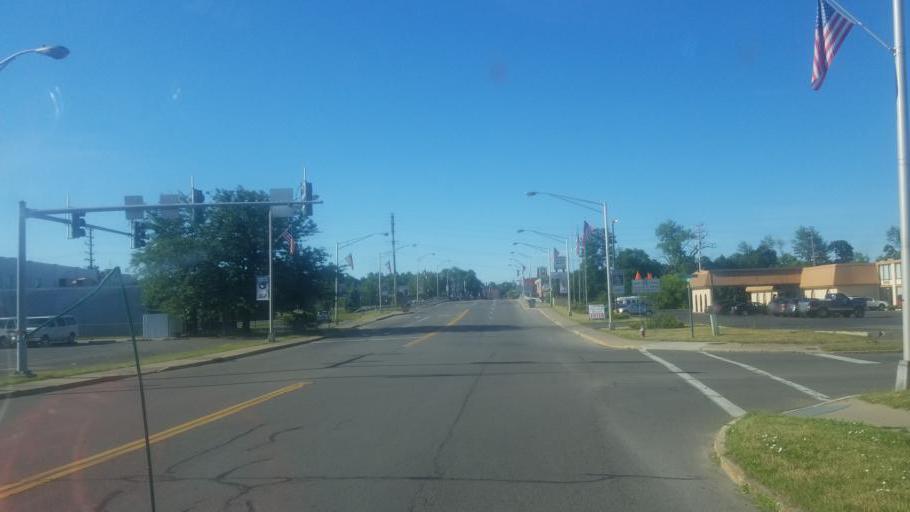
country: US
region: New York
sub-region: Wayne County
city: Newark
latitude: 43.0488
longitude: -77.0954
